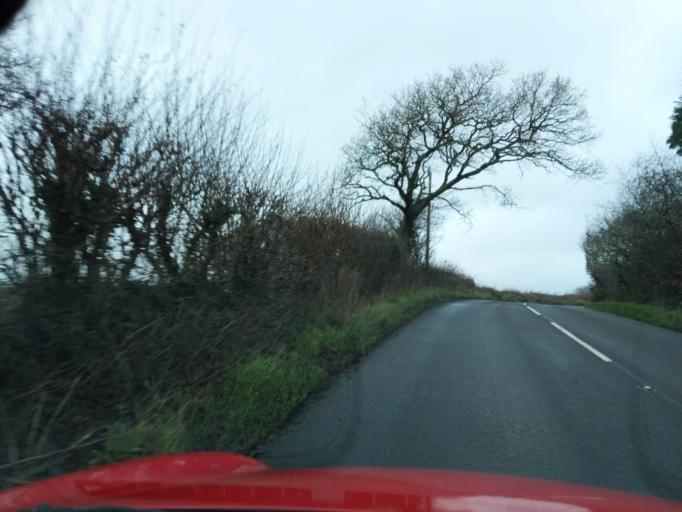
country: GB
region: England
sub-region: Devon
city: Holsworthy
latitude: 50.7945
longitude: -4.3407
